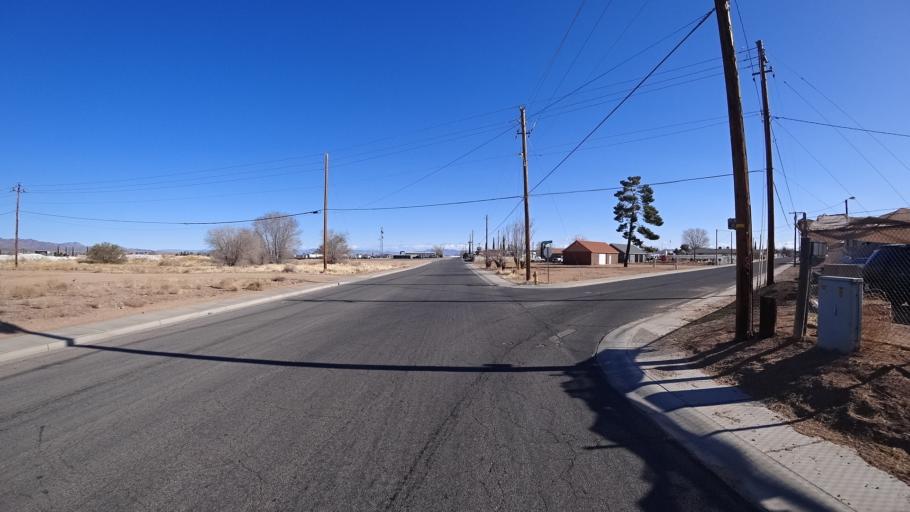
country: US
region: Arizona
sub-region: Mohave County
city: Kingman
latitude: 35.2007
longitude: -114.0217
